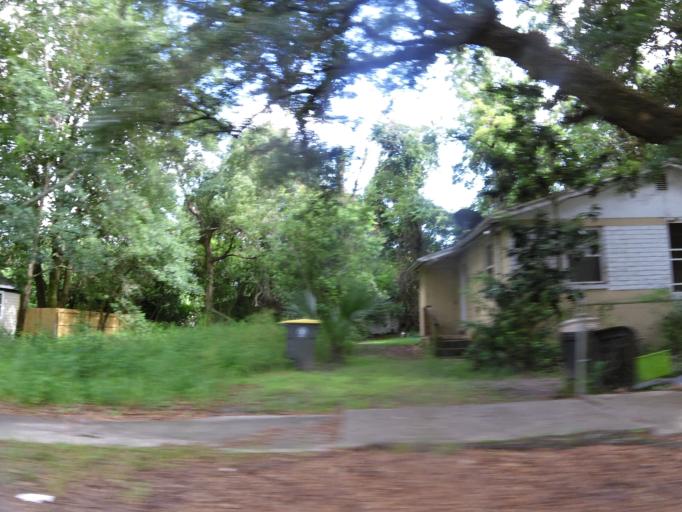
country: US
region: Florida
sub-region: Duval County
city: Jacksonville
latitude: 30.3620
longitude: -81.6880
